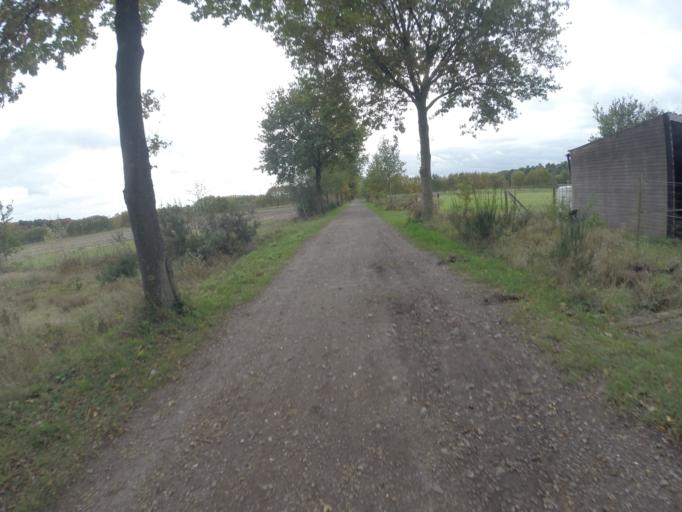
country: BE
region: Flanders
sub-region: Provincie Oost-Vlaanderen
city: Maldegem
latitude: 51.1638
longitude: 3.4598
